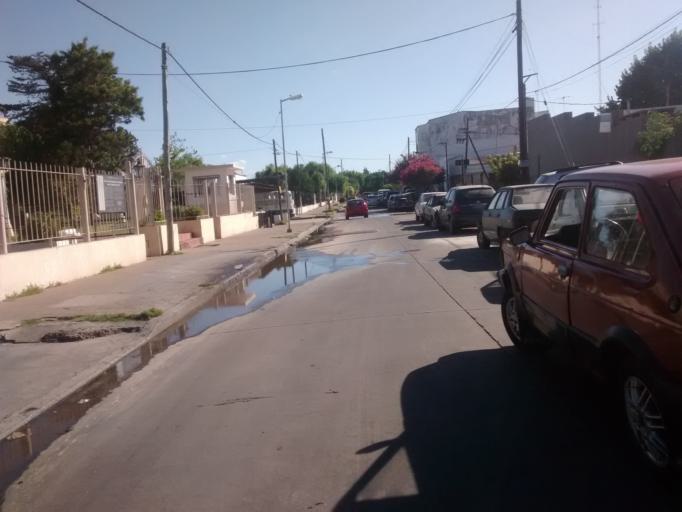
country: AR
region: Buenos Aires
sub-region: Partido de La Plata
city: La Plata
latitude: -34.9364
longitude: -57.9266
